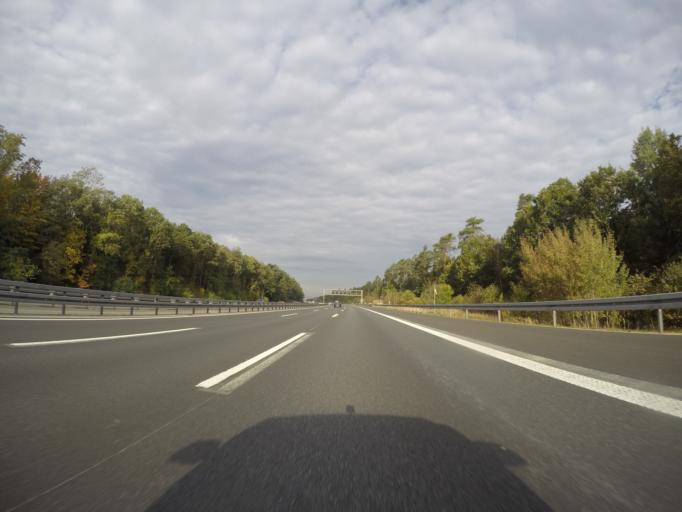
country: DE
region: Bavaria
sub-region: Regierungsbezirk Mittelfranken
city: Heroldsberg
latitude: 49.5065
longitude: 11.1182
